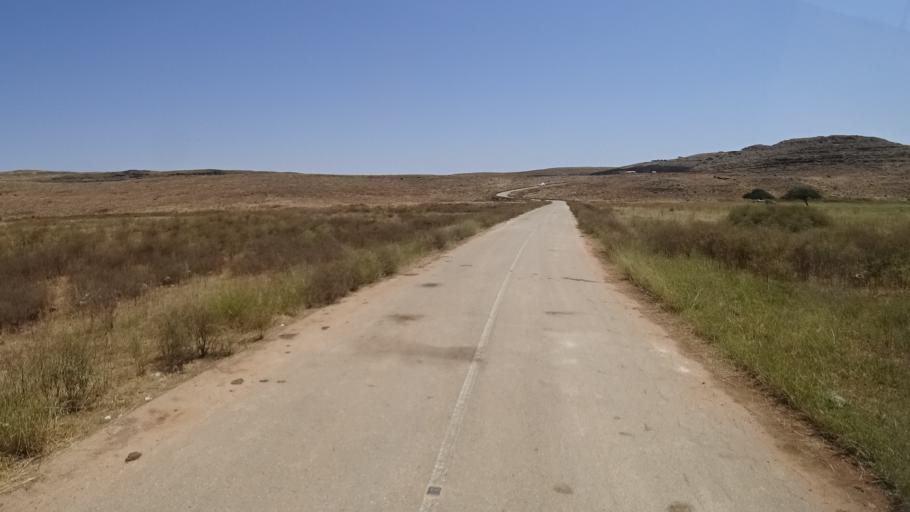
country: OM
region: Zufar
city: Salalah
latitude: 17.1551
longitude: 54.6183
